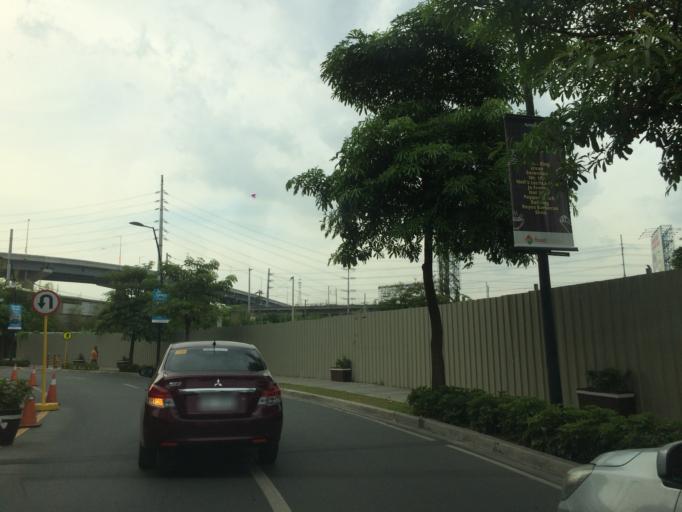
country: PH
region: Calabarzon
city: Del Monte
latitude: 14.6556
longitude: 121.0014
